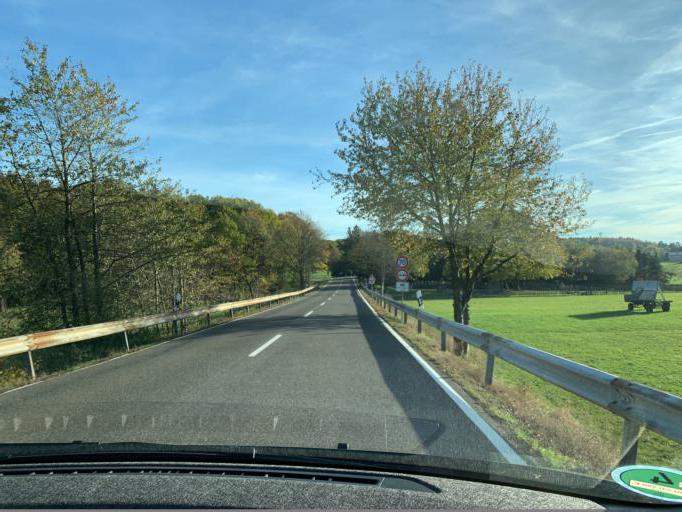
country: DE
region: North Rhine-Westphalia
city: Heimbach
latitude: 50.5951
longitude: 6.4944
